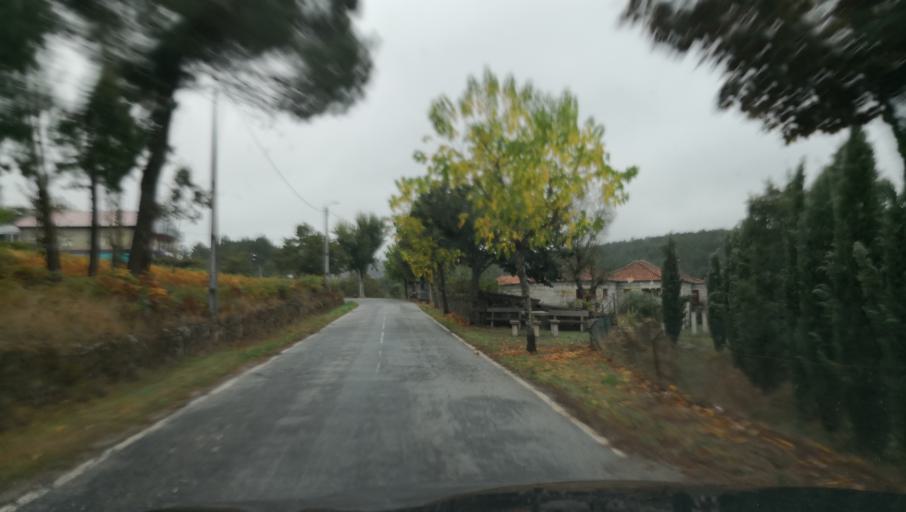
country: PT
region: Vila Real
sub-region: Sabrosa
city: Sabrosa
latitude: 41.3522
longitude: -7.5854
